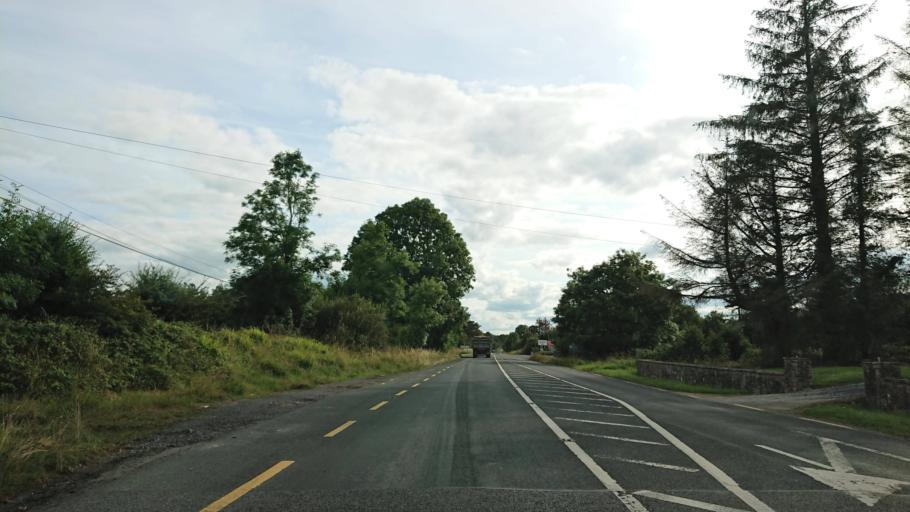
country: IE
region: Connaught
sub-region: County Leitrim
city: Carrick-on-Shannon
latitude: 53.9730
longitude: -8.0625
